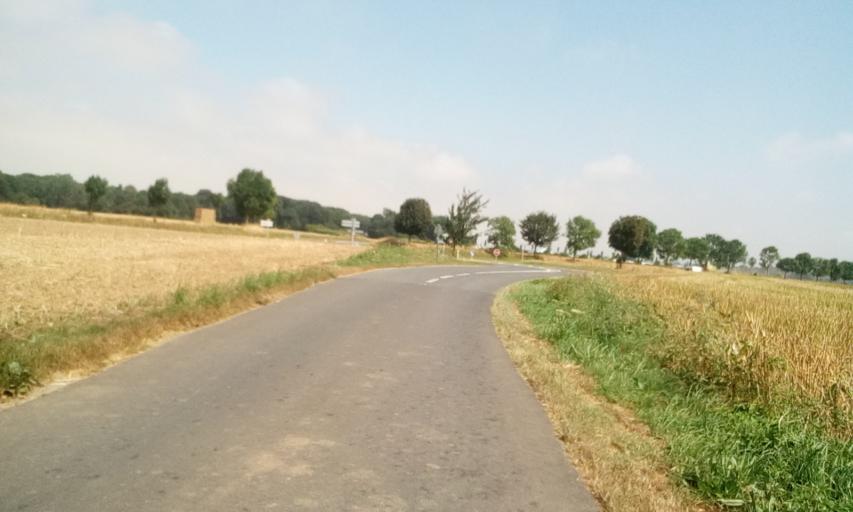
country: FR
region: Lower Normandy
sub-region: Departement du Calvados
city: Bernieres-sur-Mer
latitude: 49.2908
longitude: -0.4204
